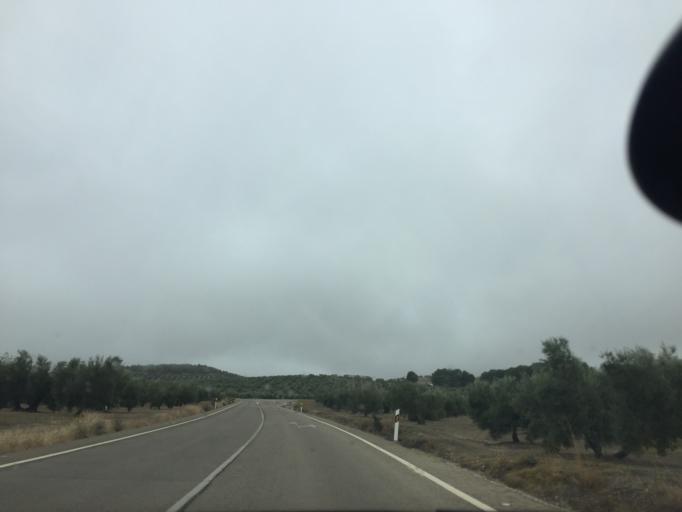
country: ES
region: Andalusia
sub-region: Provincia de Jaen
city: Jimena
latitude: 37.8394
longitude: -3.5325
